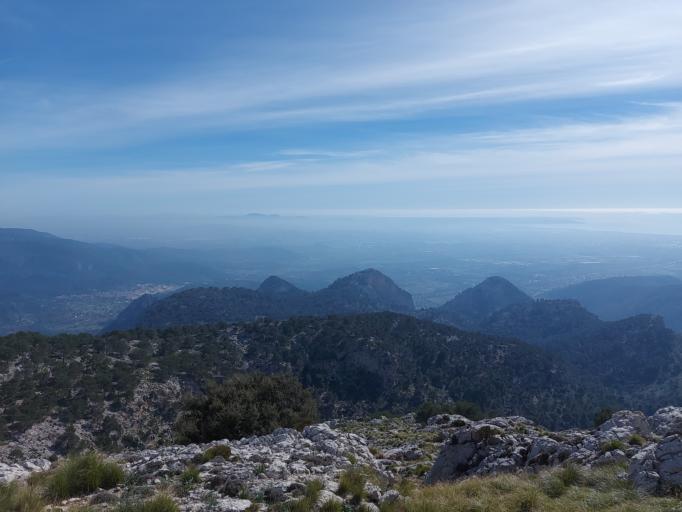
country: ES
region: Balearic Islands
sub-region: Illes Balears
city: Deia
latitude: 39.7143
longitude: 2.6589
